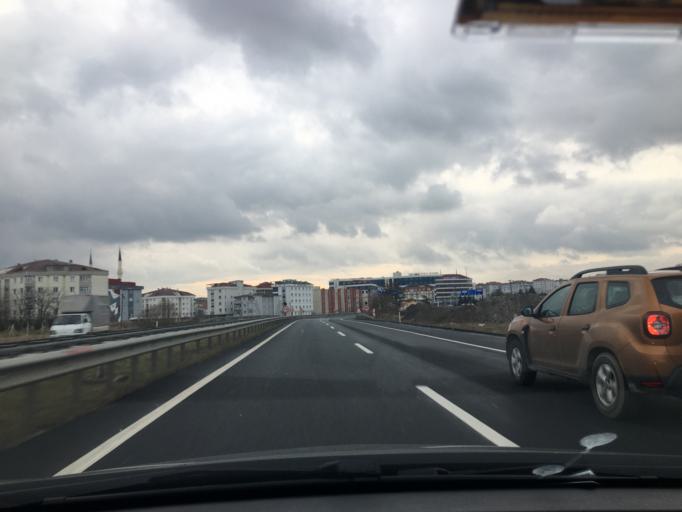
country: TR
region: Tekirdag
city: Cerkezkoey
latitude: 41.2813
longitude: 28.0175
